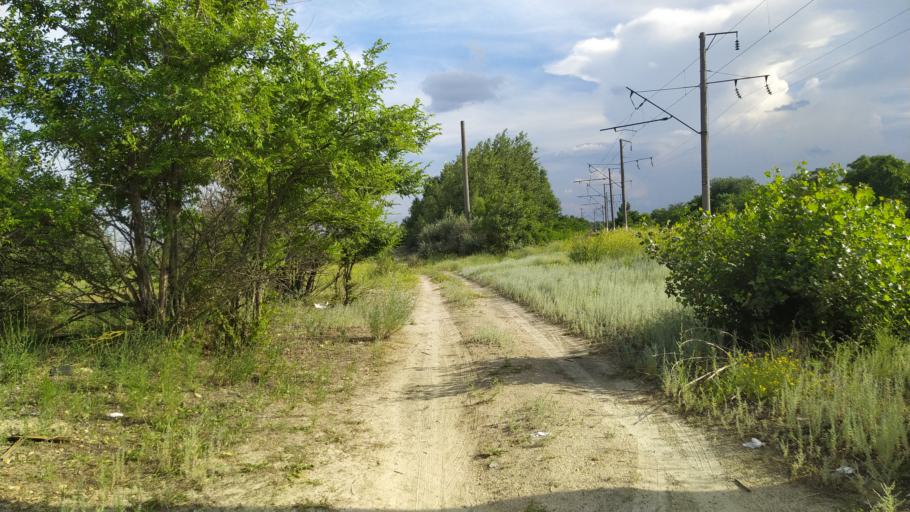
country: RU
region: Rostov
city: Bataysk
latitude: 47.1201
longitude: 39.7130
